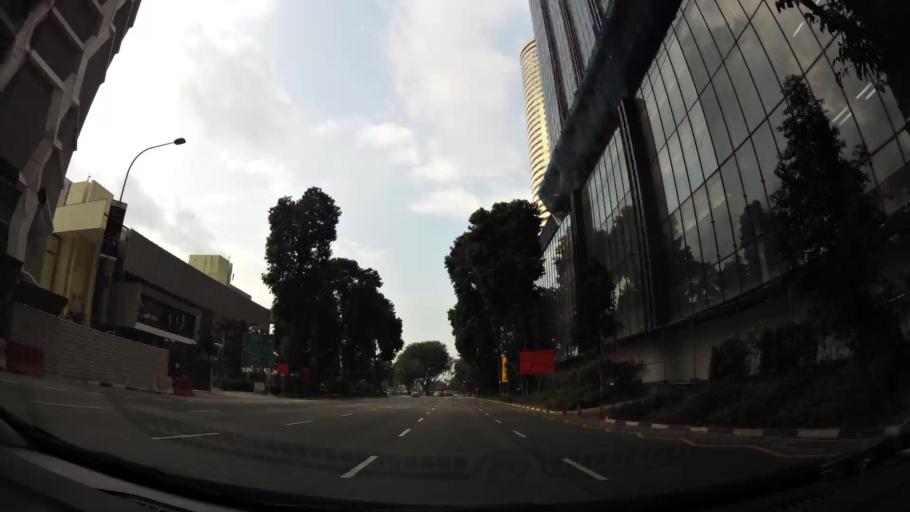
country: SG
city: Singapore
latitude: 1.2771
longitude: 103.8489
